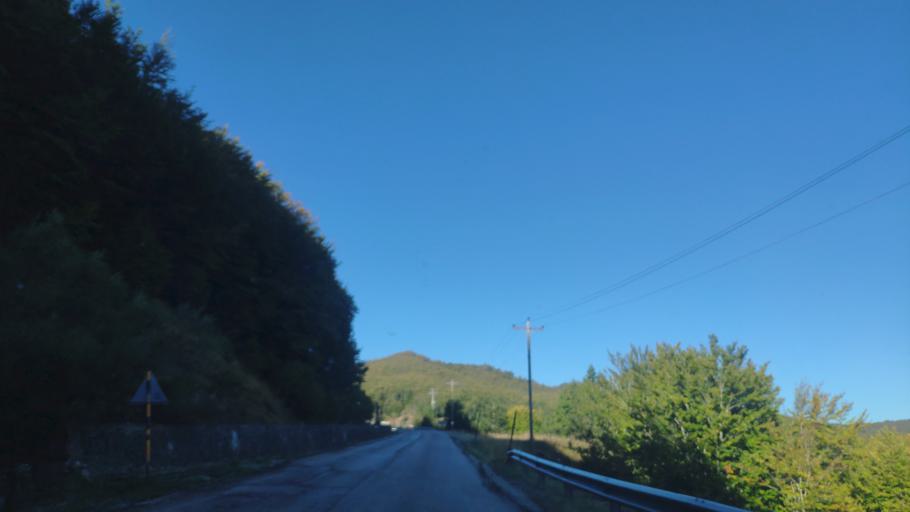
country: GR
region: Epirus
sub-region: Nomos Ioanninon
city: Metsovo
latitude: 39.7795
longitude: 21.1674
